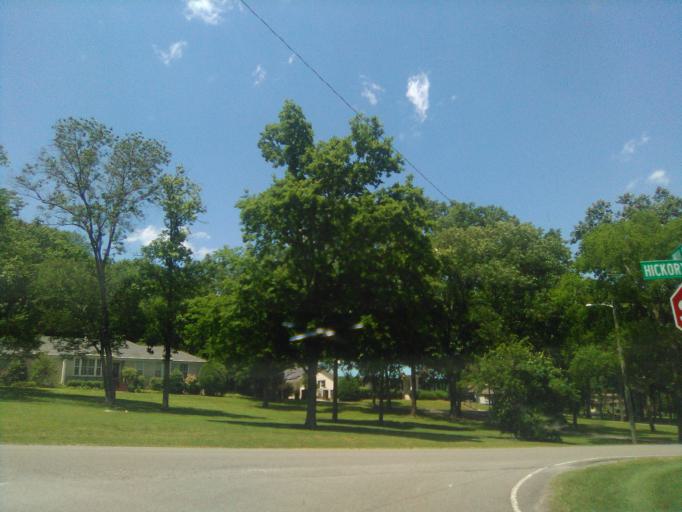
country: US
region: Tennessee
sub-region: Davidson County
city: Belle Meade
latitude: 36.1298
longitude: -86.8696
